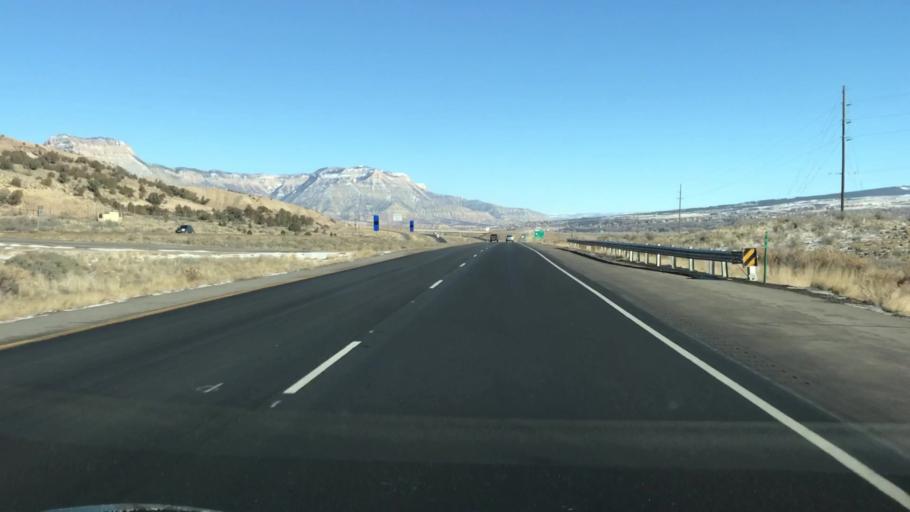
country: US
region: Colorado
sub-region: Garfield County
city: Parachute
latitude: 39.4209
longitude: -108.0865
